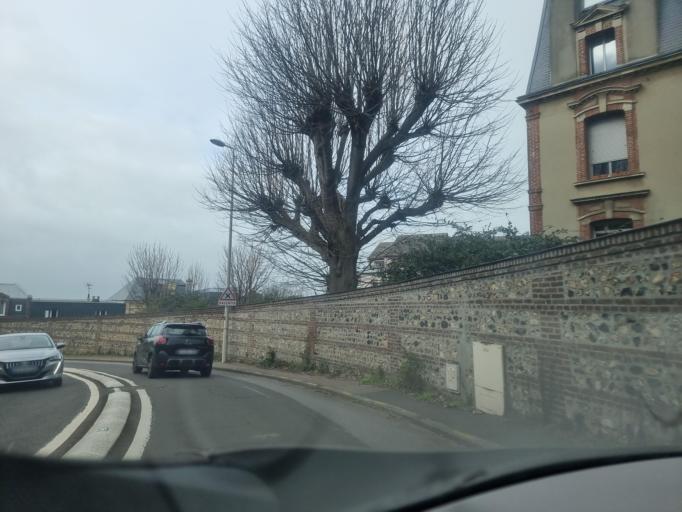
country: FR
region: Haute-Normandie
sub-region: Departement de la Seine-Maritime
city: Le Havre
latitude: 49.5005
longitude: 0.0975
